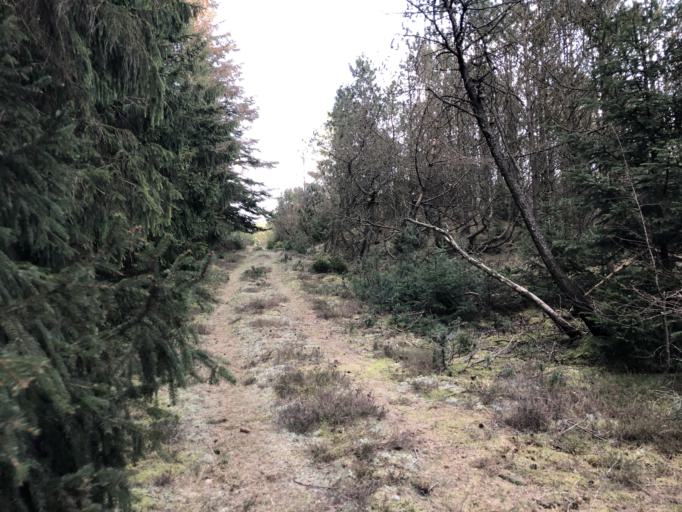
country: DK
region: Central Jutland
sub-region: Holstebro Kommune
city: Ulfborg
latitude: 56.2474
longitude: 8.4482
